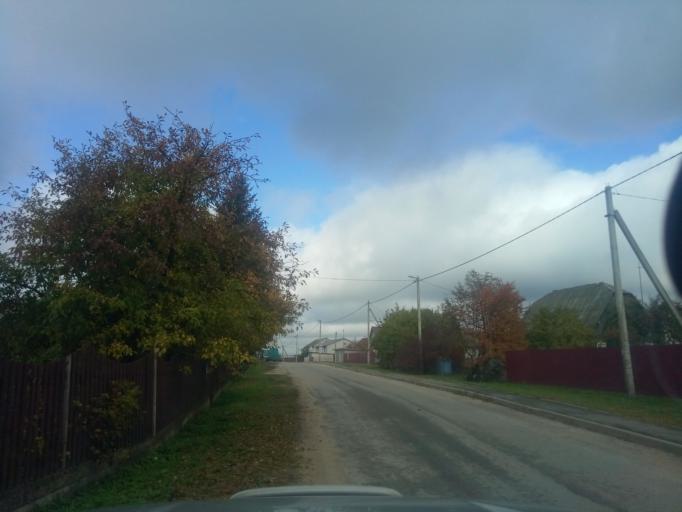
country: BY
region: Minsk
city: Zaslawye
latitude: 54.0151
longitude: 27.2914
